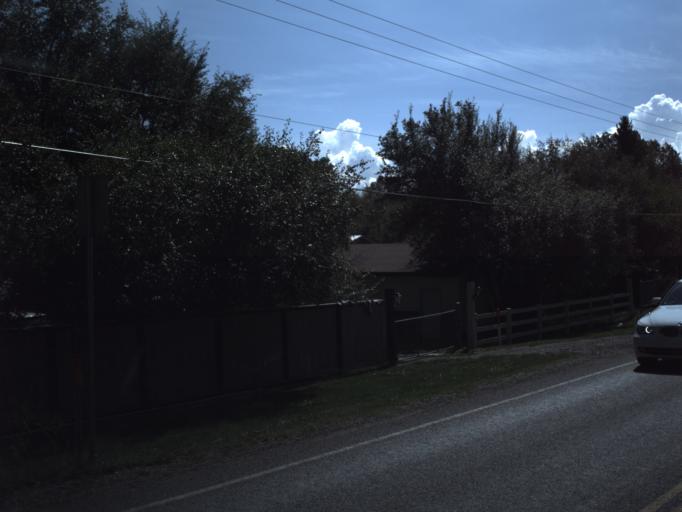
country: US
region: Idaho
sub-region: Bear Lake County
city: Paris
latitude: 41.9274
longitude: -111.3970
